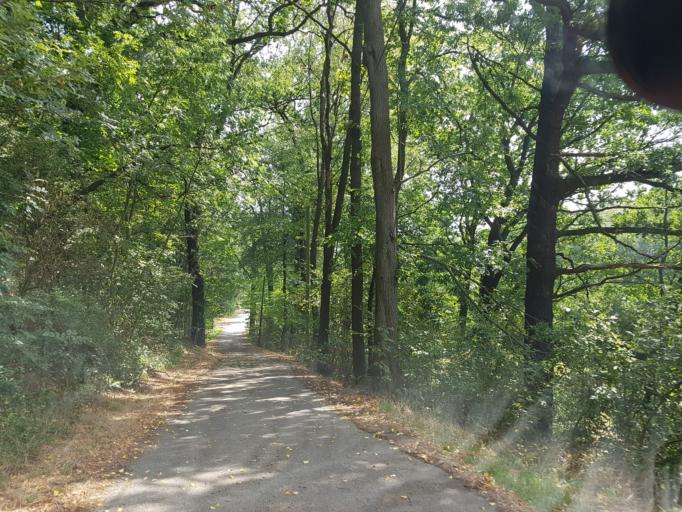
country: DE
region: Saxony
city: Waldheim
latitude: 51.0642
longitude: 13.0032
